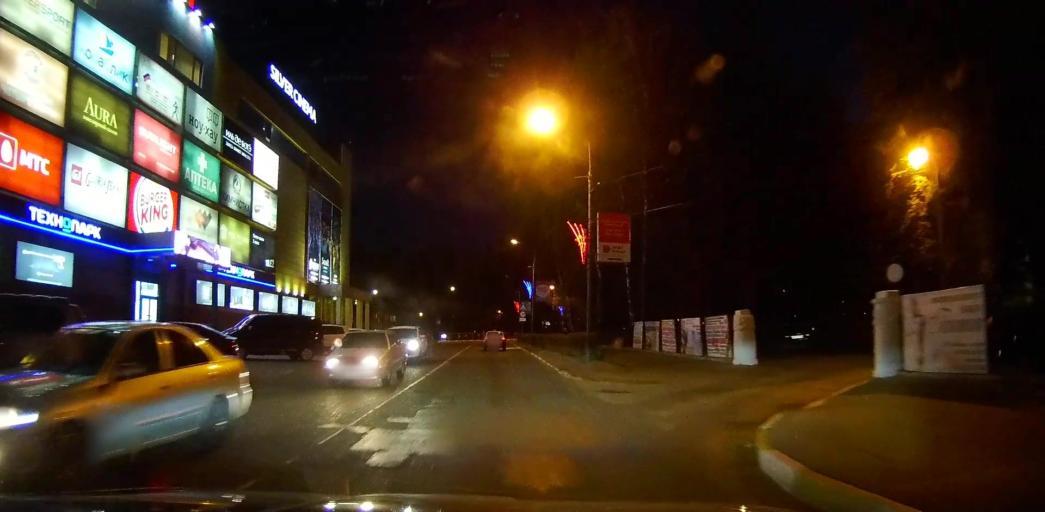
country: RU
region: Moskovskaya
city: Voskresensk
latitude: 55.3221
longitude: 38.6726
